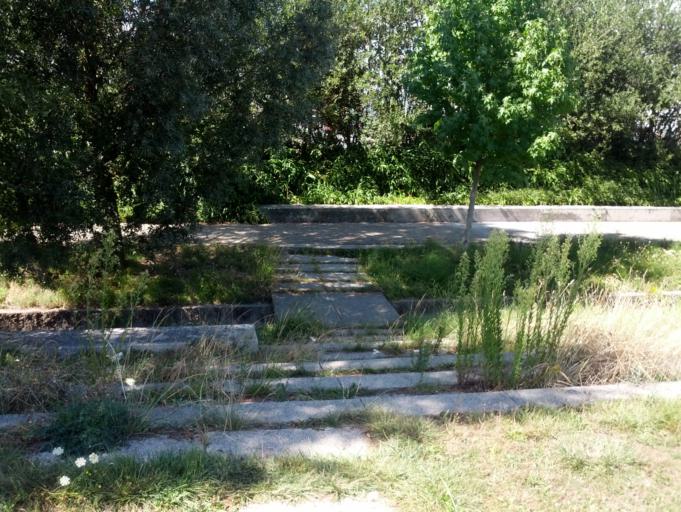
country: FR
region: Aquitaine
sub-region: Departement de la Gironde
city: Floirac
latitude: 44.8265
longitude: -0.5300
